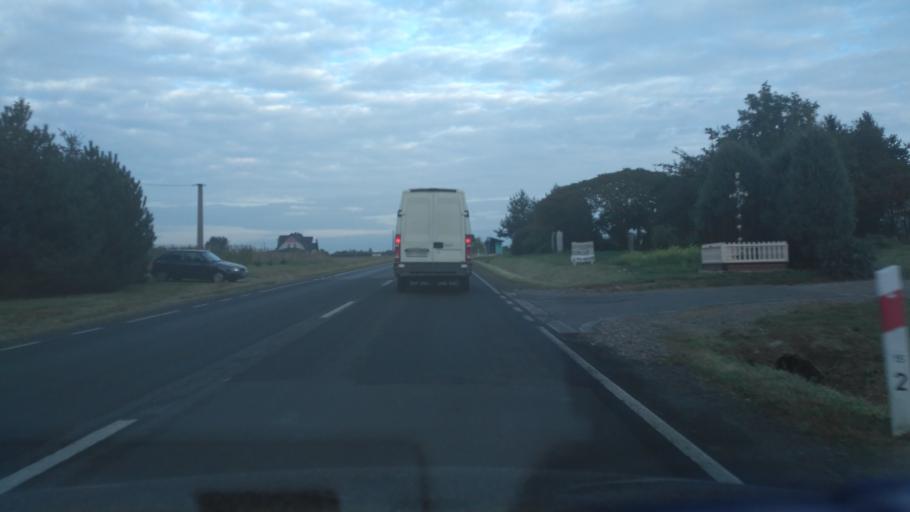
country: PL
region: Lublin Voivodeship
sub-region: Powiat leczynski
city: Spiczyn
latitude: 51.3001
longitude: 22.7592
